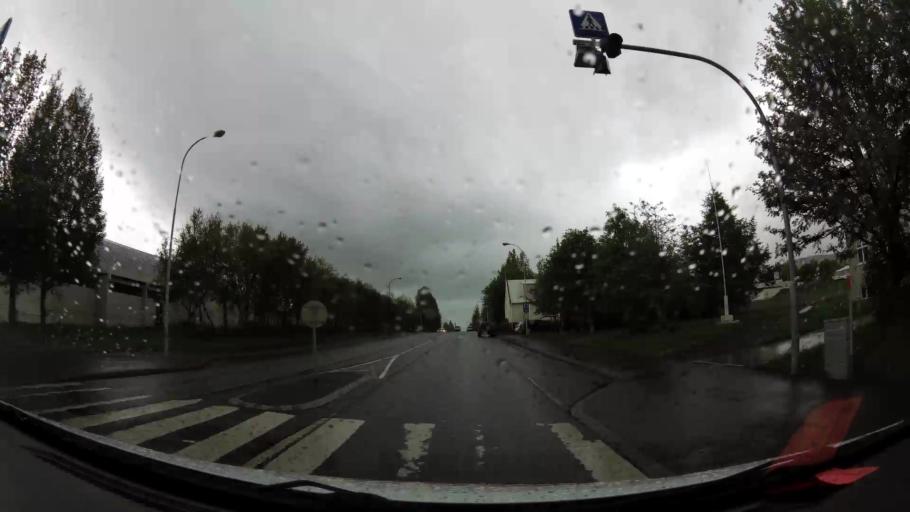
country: IS
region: Northeast
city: Akureyri
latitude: 65.6782
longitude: -18.0992
